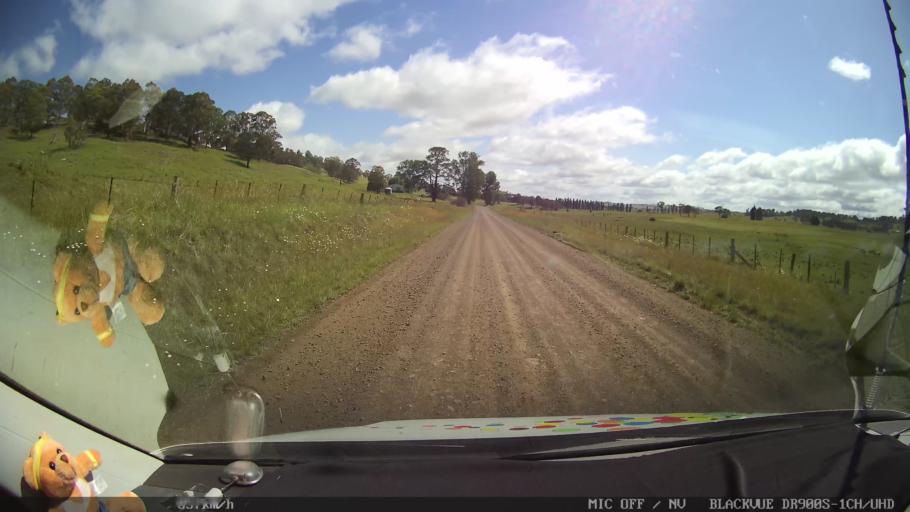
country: AU
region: New South Wales
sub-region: Glen Innes Severn
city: Glen Innes
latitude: -29.9528
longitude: 151.7056
